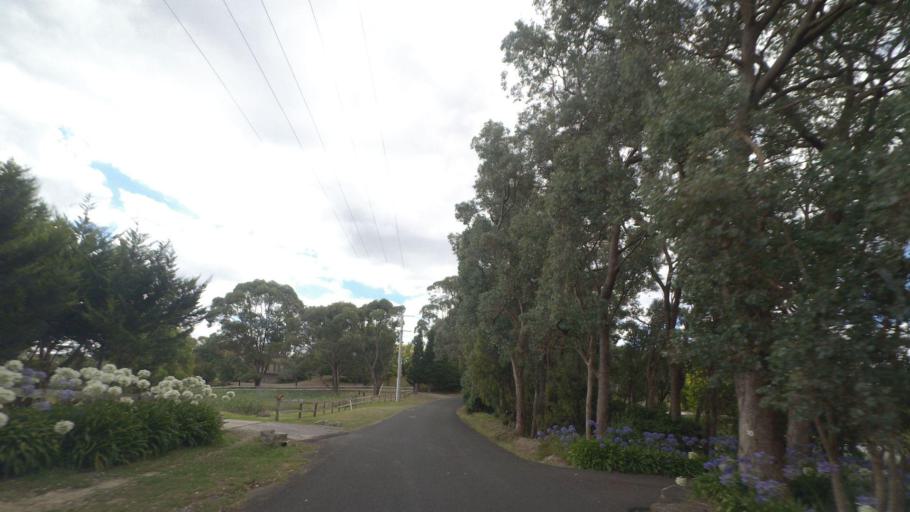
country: AU
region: Victoria
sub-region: Manningham
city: Warrandyte
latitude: -37.7560
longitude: 145.2506
